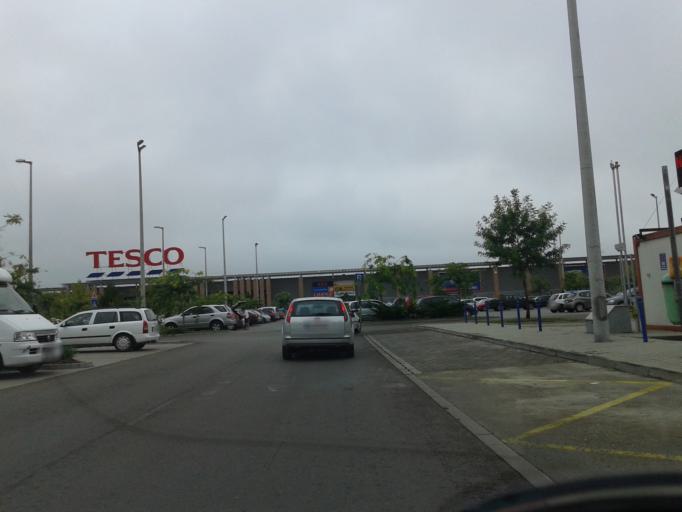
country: HU
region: Csongrad
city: Szeged
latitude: 46.2428
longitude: 20.1217
